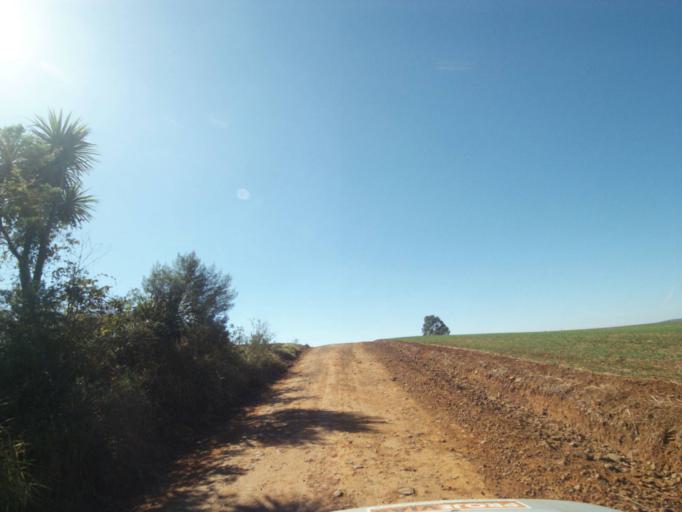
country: BR
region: Parana
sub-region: Tibagi
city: Tibagi
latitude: -24.5632
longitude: -50.6253
